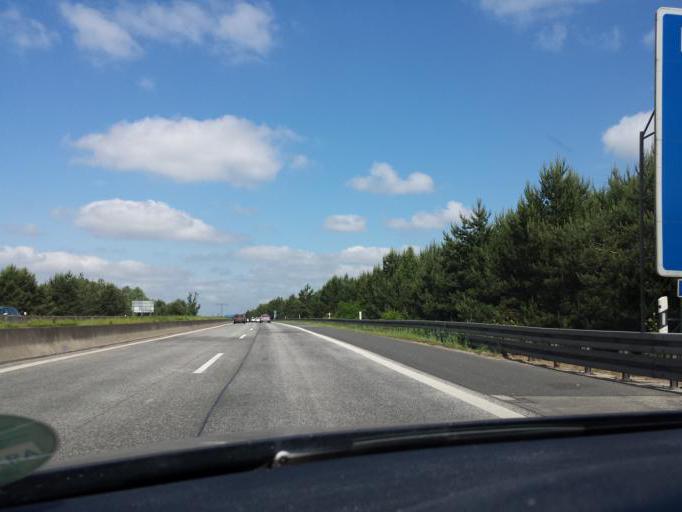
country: DE
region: Brandenburg
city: Hohen Neuendorf
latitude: 52.6732
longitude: 13.2334
